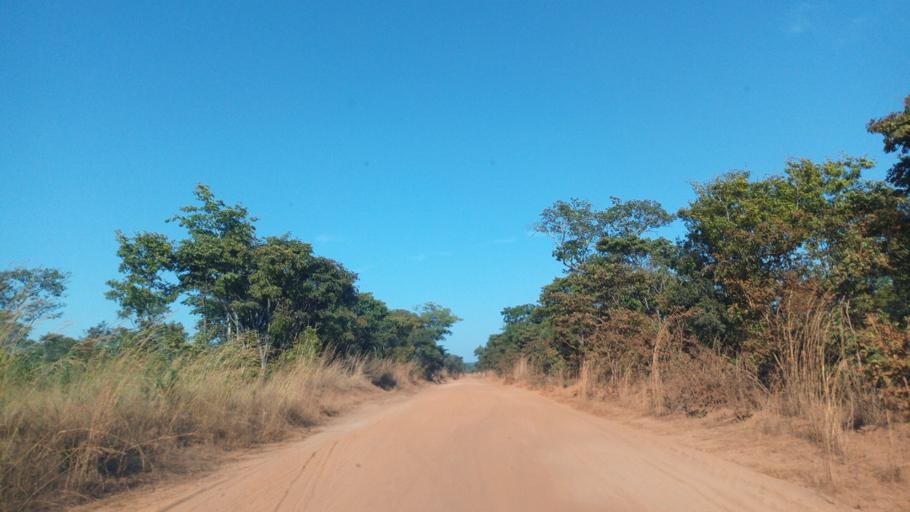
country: ZM
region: Luapula
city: Mwense
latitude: -10.6031
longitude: 28.4217
